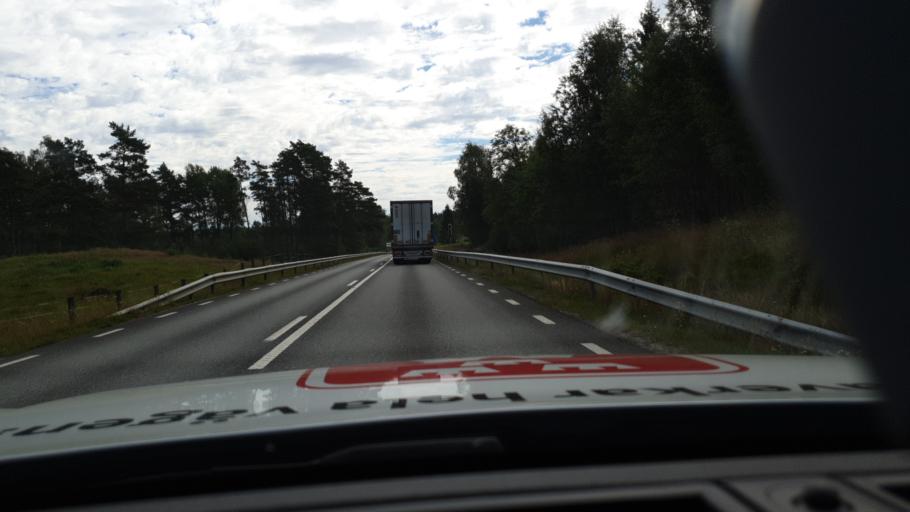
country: SE
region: Joenkoeping
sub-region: Savsjo Kommun
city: Vrigstad
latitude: 57.3686
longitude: 14.4252
